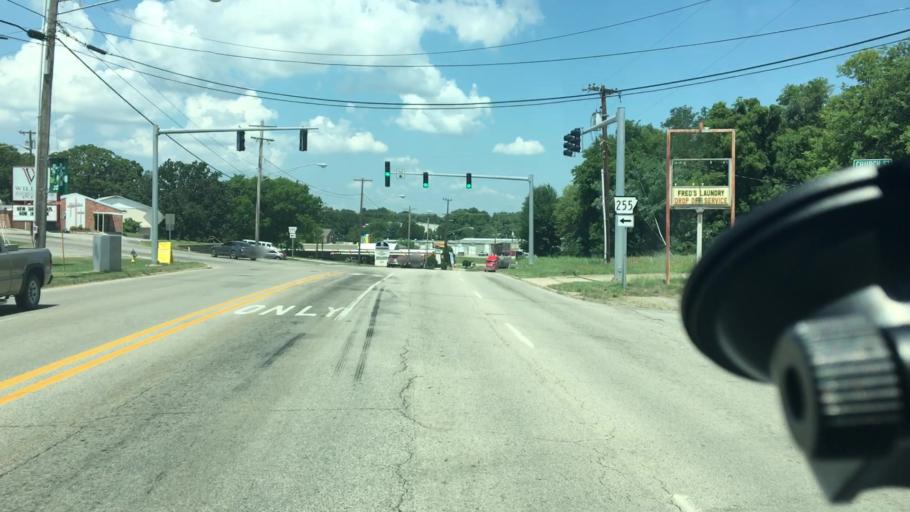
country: US
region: Arkansas
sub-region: Sebastian County
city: Barling
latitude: 35.3252
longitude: -94.3011
